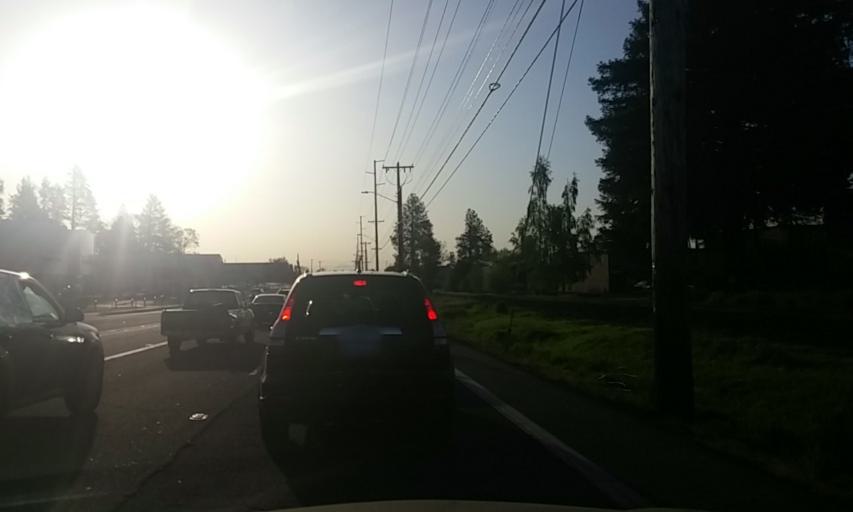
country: US
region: Oregon
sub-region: Washington County
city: Beaverton
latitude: 45.4889
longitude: -122.8205
